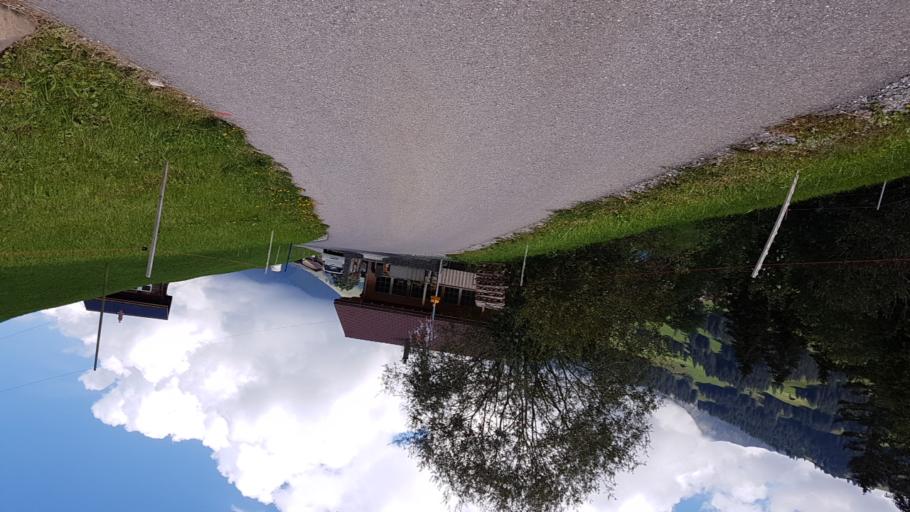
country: CH
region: Bern
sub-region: Frutigen-Niedersimmental District
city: Adelboden
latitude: 46.4918
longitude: 7.5812
